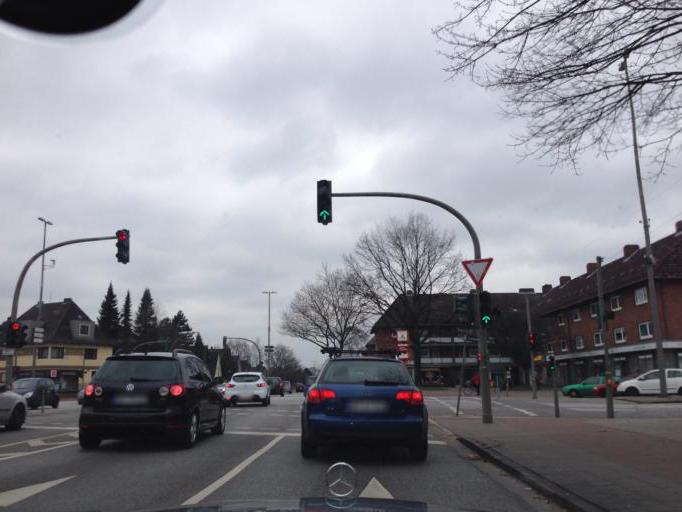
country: DE
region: Hamburg
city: Steilshoop
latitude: 53.6088
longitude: 10.0732
